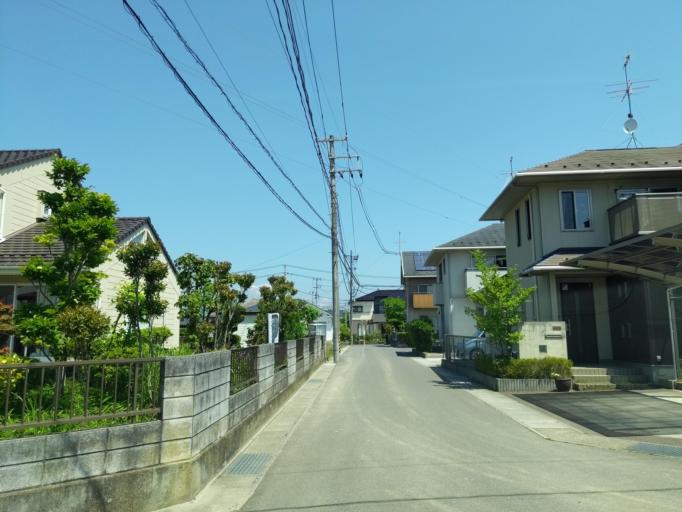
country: JP
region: Fukushima
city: Koriyama
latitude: 37.3818
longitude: 140.3494
